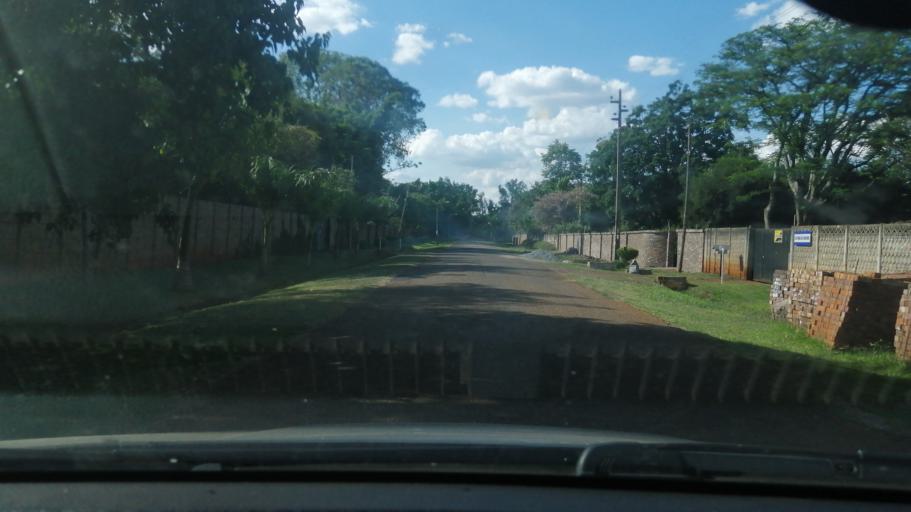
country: ZW
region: Harare
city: Harare
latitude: -17.7675
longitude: 31.0617
